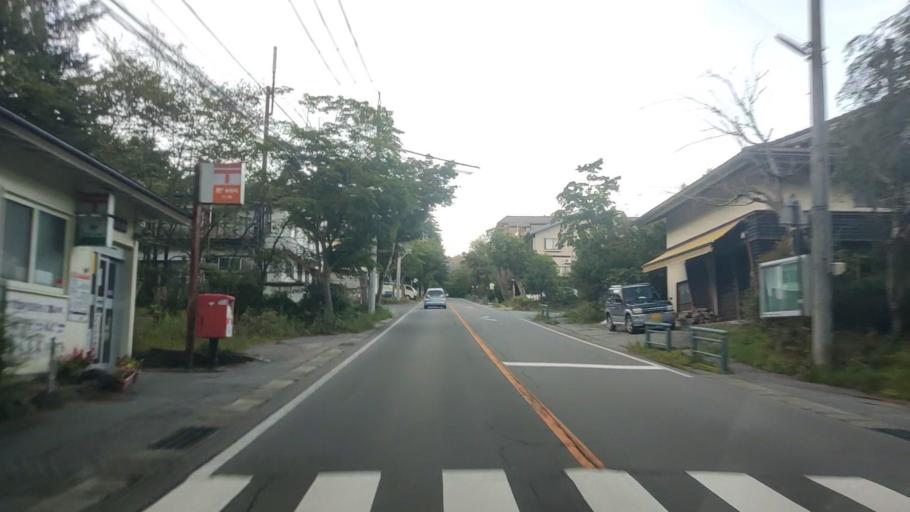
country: JP
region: Nagano
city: Komoro
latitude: 36.3721
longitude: 138.5877
